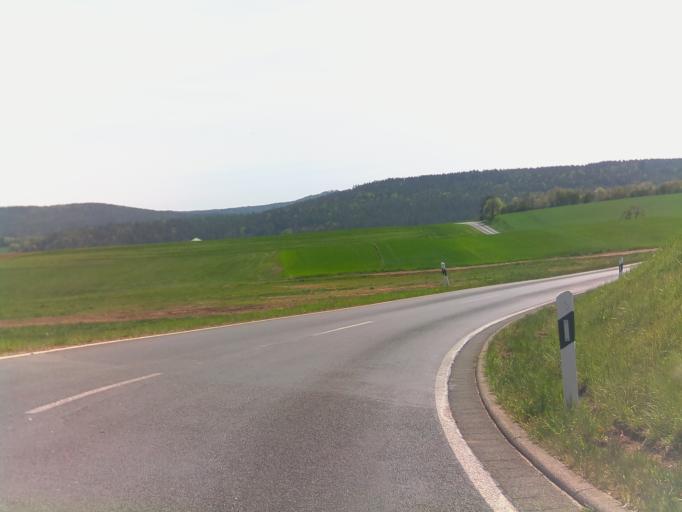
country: DE
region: Bavaria
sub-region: Regierungsbezirk Unterfranken
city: Burgpreppach
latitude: 50.1654
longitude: 10.6350
